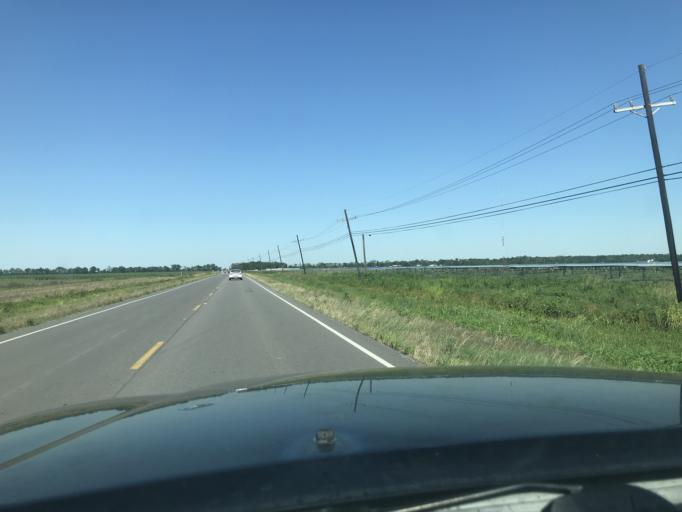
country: US
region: Louisiana
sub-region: West Baton Rouge Parish
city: Erwinville
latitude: 30.4686
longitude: -91.3387
